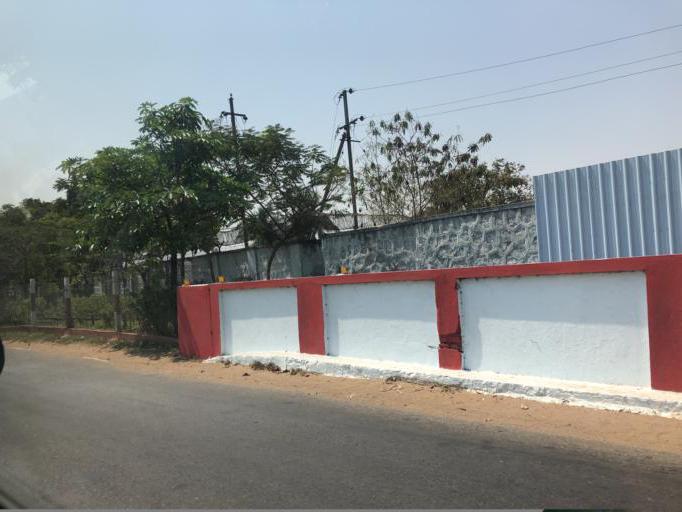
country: IN
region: Andhra Pradesh
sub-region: Vishakhapatnam
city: Yarada
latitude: 17.6958
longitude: 83.2687
